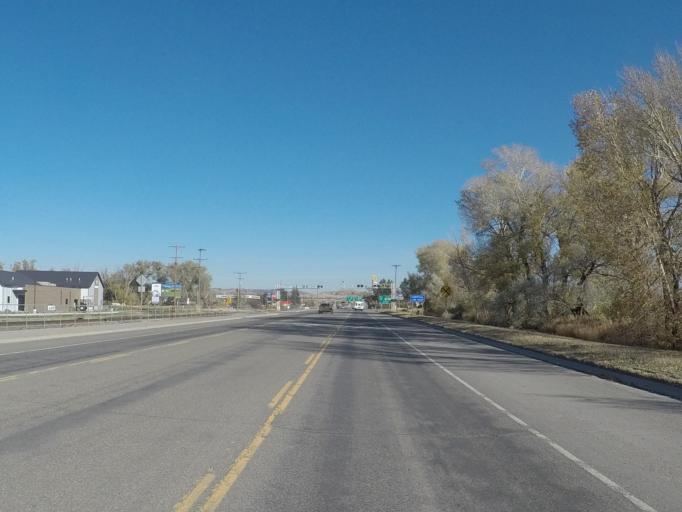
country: US
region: Montana
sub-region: Park County
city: Livingston
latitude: 45.6387
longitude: -110.5748
